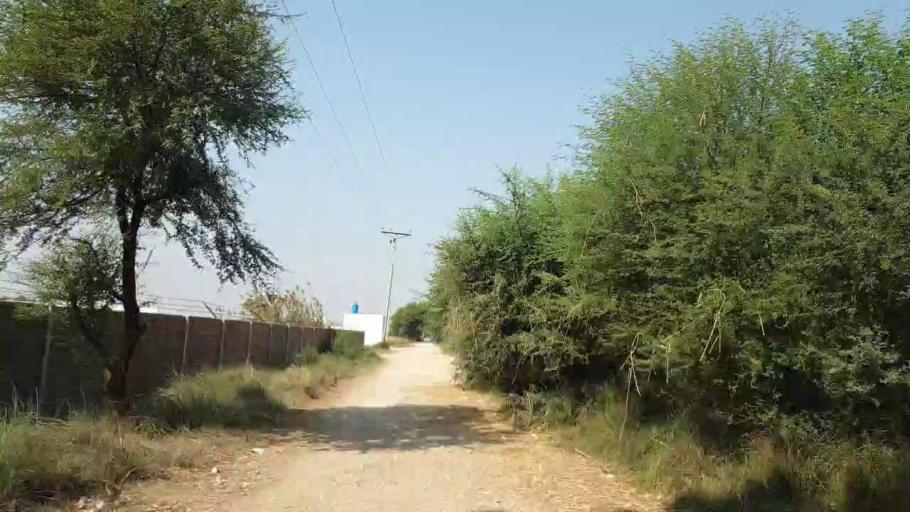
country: PK
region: Sindh
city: Tando Muhammad Khan
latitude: 25.0228
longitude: 68.4116
